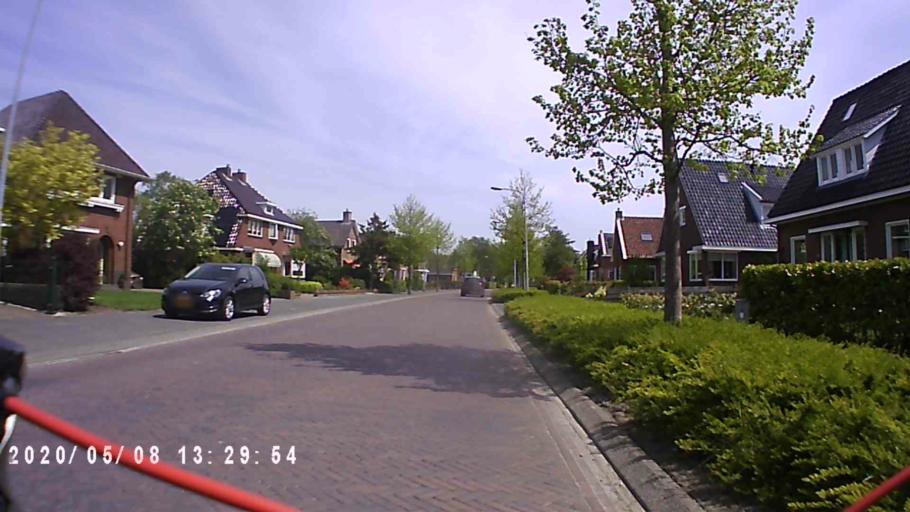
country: NL
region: Groningen
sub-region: Gemeente Appingedam
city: Appingedam
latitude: 53.3319
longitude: 6.7396
